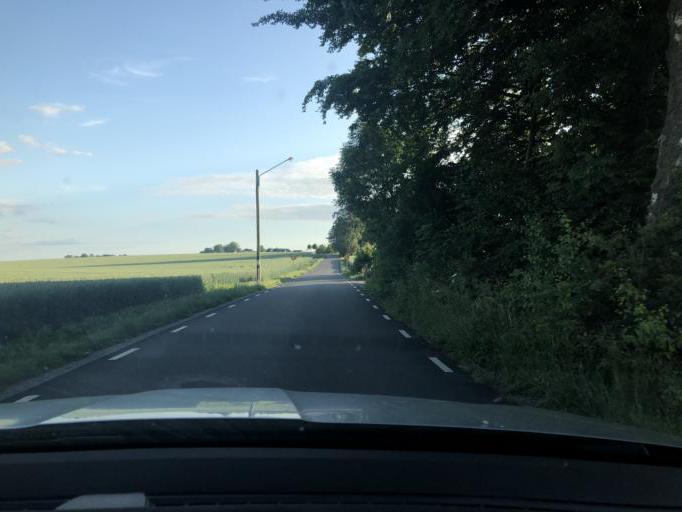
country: SE
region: Skane
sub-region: Simrishamns Kommun
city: Simrishamn
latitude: 55.4959
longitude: 14.2026
